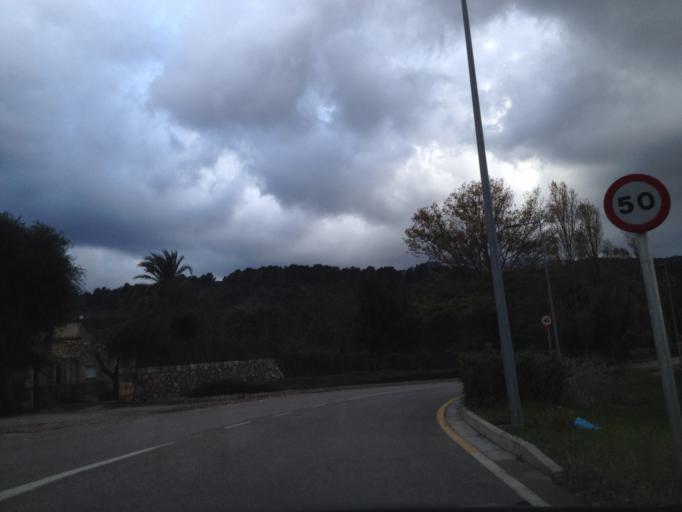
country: ES
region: Balearic Islands
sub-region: Illes Balears
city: Pollenca
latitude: 39.8702
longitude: 3.0133
